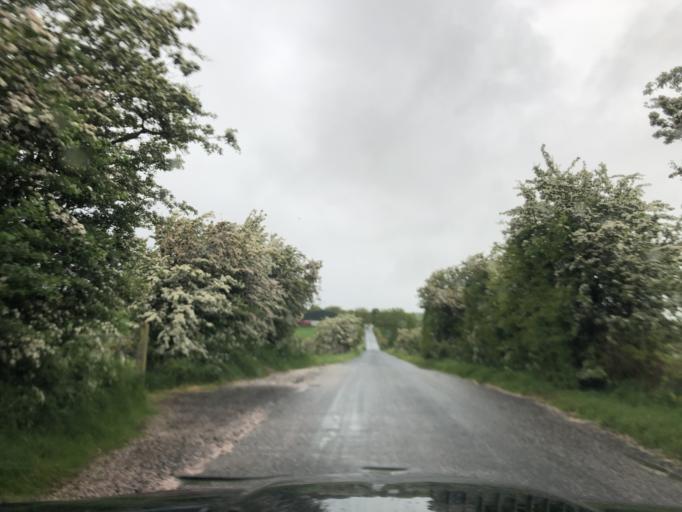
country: GB
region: Northern Ireland
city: Dunloy
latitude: 55.1289
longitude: -6.3710
